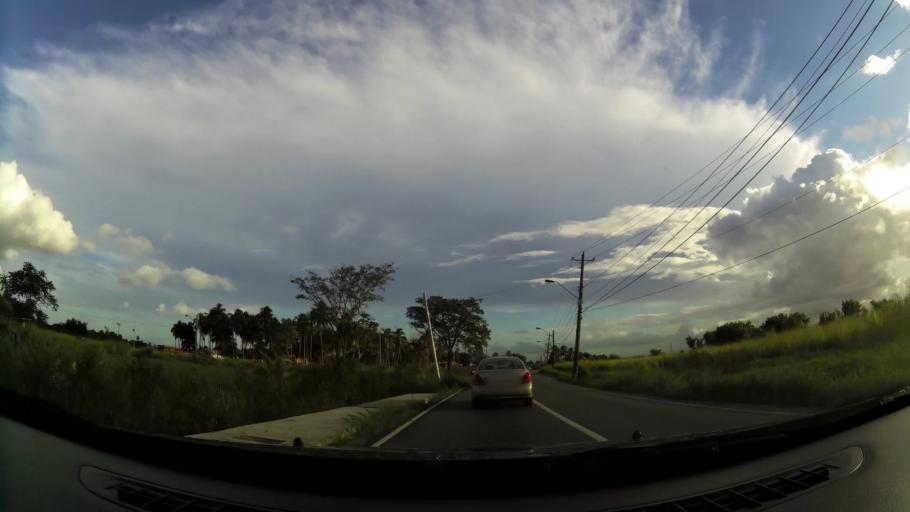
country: TT
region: Tunapuna/Piarco
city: Tunapuna
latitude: 10.5957
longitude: -61.3680
